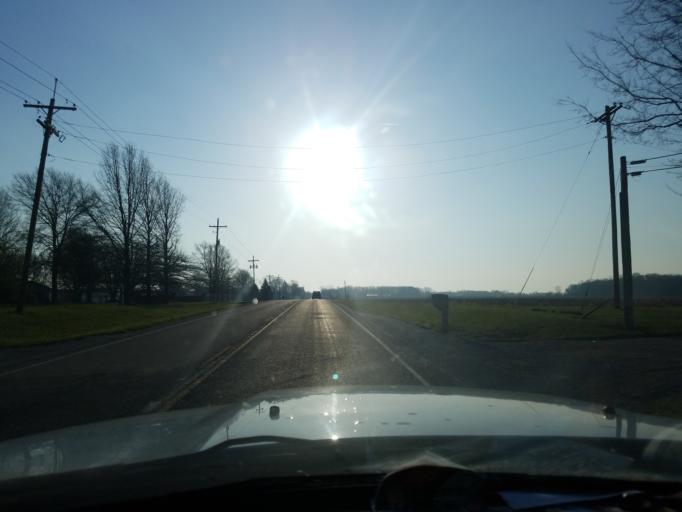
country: US
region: Indiana
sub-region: Vigo County
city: Seelyville
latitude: 39.3902
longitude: -87.2800
